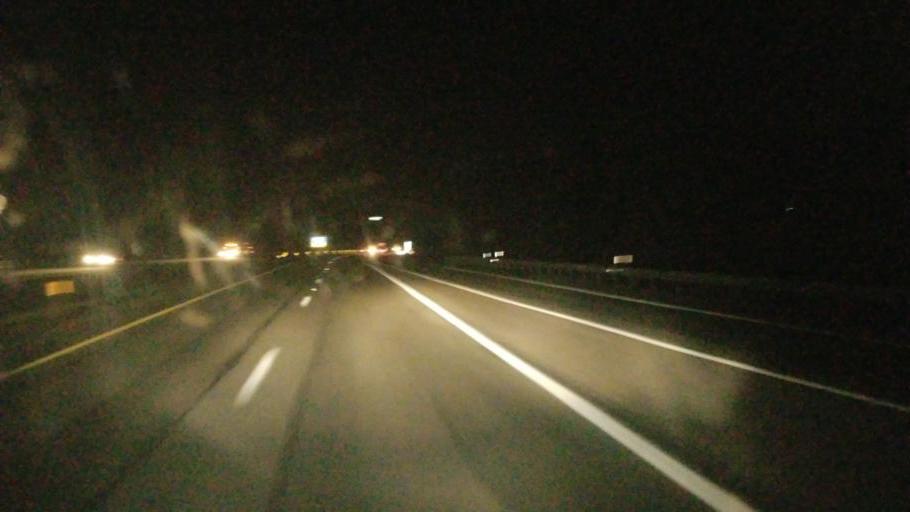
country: US
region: West Virginia
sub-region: Ohio County
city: West Liberty
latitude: 40.1014
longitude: -80.5040
